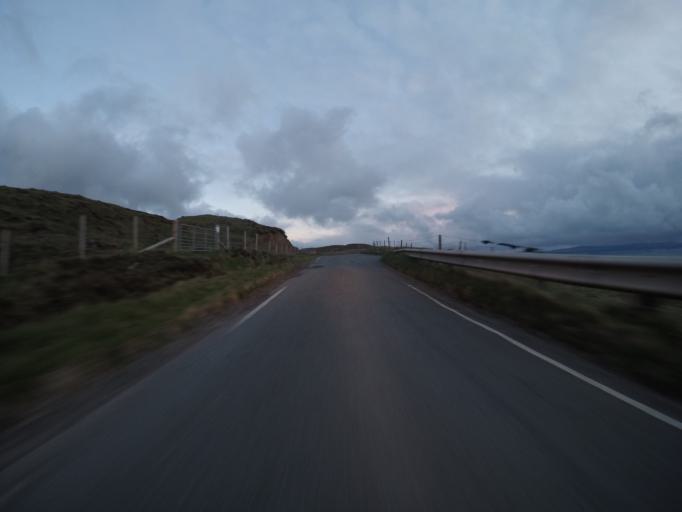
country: GB
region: Scotland
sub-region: Highland
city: Portree
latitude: 57.6047
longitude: -6.3764
